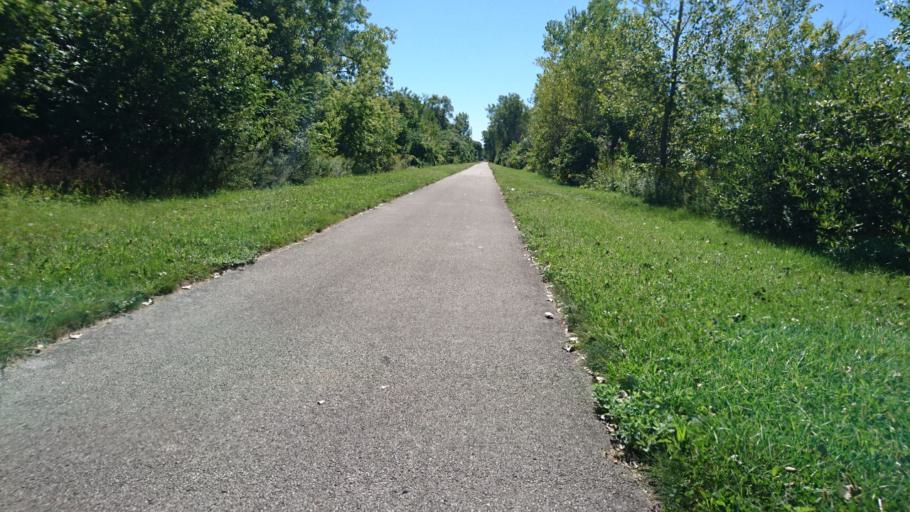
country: US
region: Illinois
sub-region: Cook County
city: Lansing
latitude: 41.5767
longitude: -87.5466
